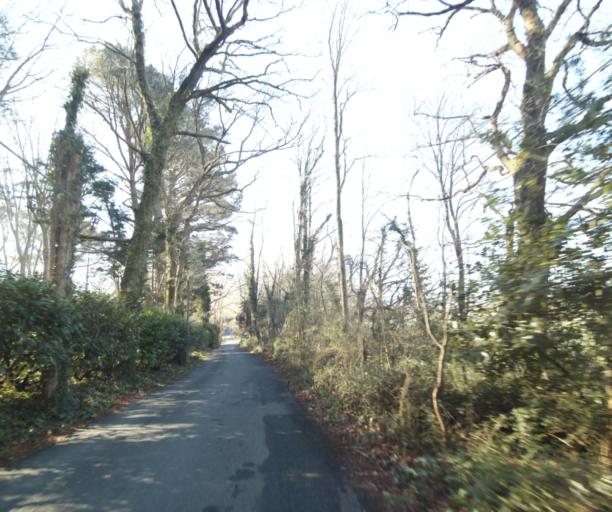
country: FR
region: Aquitaine
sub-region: Departement des Pyrenees-Atlantiques
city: Ciboure
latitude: 43.3647
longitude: -1.6607
